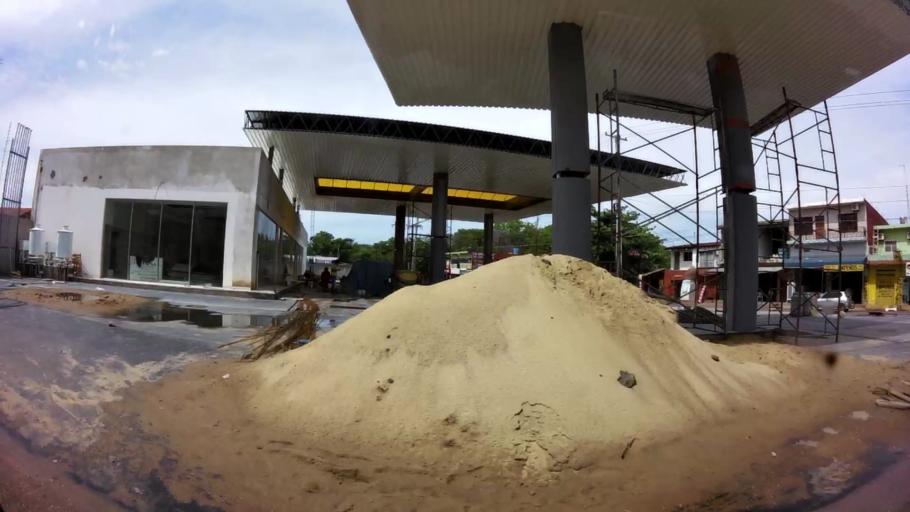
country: PY
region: Central
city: Limpio
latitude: -25.1856
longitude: -57.4649
